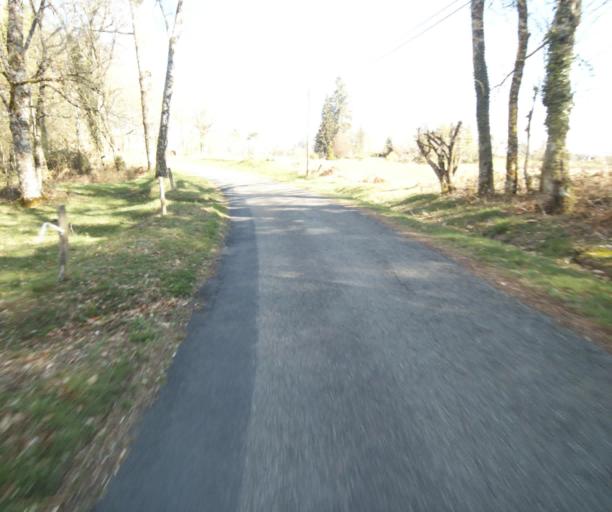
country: FR
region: Limousin
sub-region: Departement de la Correze
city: Laguenne
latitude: 45.2406
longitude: 1.9182
